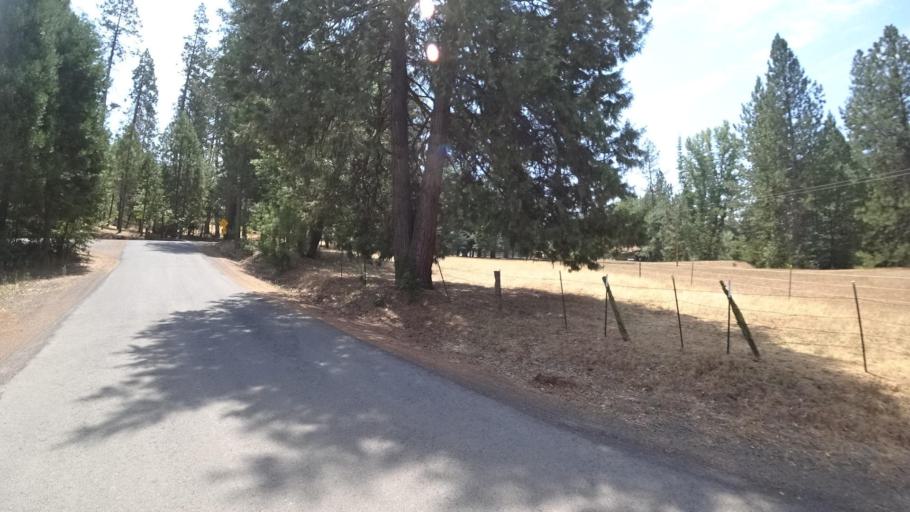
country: US
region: California
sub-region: Mariposa County
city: Midpines
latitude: 37.7198
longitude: -120.0936
